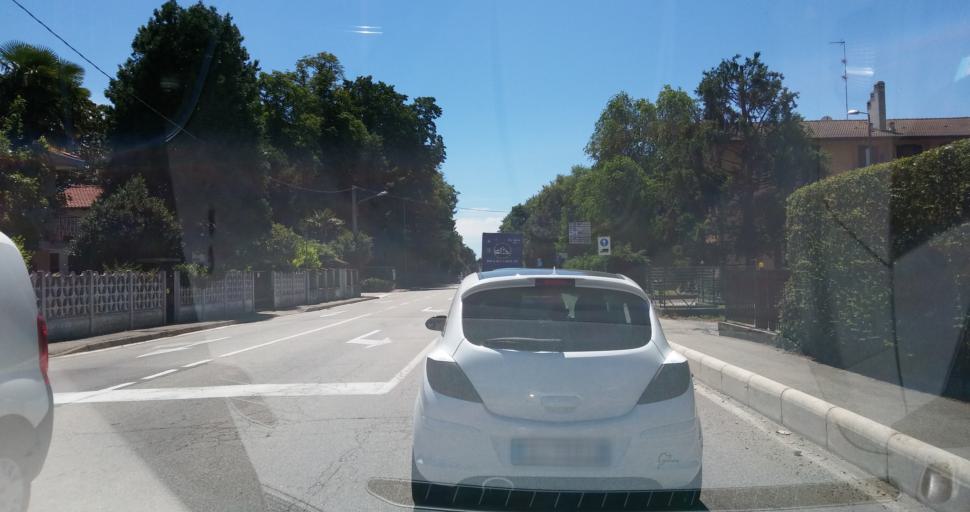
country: IT
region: Lombardy
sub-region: Provincia di Varese
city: Somma Lombardo
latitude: 45.6883
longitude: 8.7020
